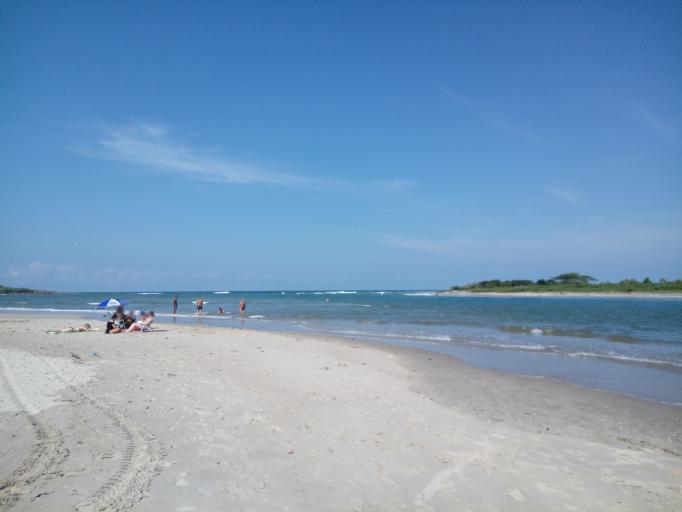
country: BR
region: Parana
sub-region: Guaratuba
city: Guaratuba
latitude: -25.9752
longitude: -48.5976
